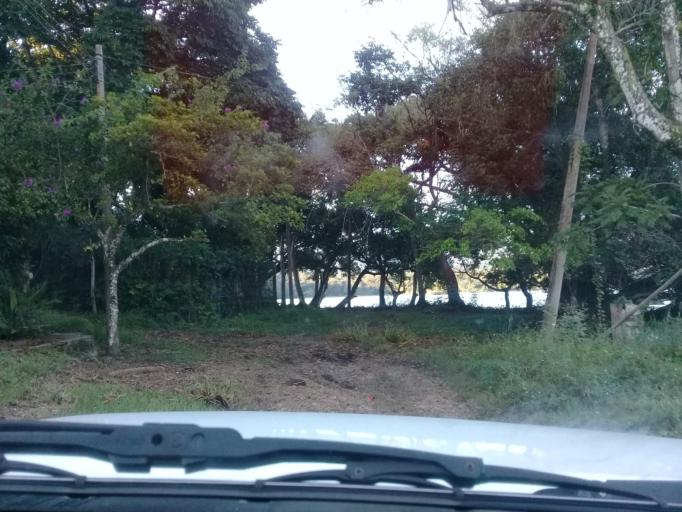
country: MX
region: Veracruz
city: Catemaco
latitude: 18.4366
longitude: -95.0805
